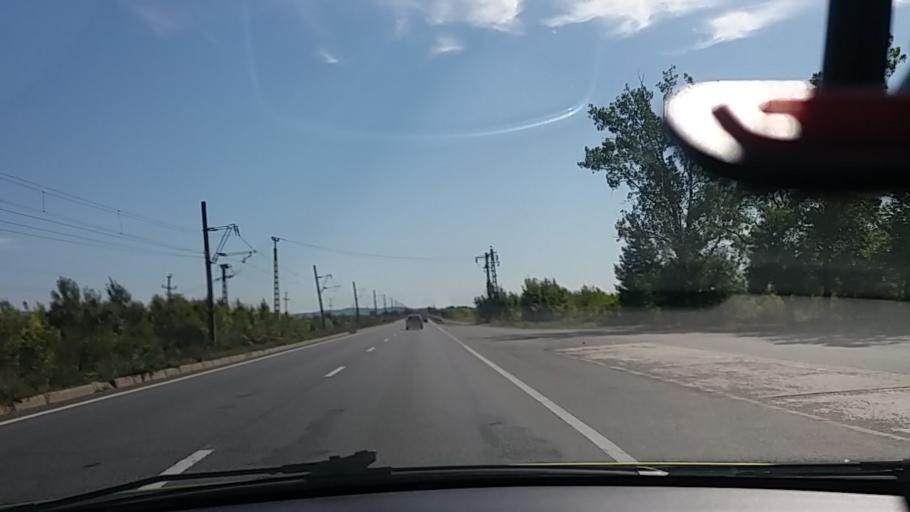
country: RO
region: Arad
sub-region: Comuna Vladimirescu
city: Mandruloc
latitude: 46.1535
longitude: 21.4429
